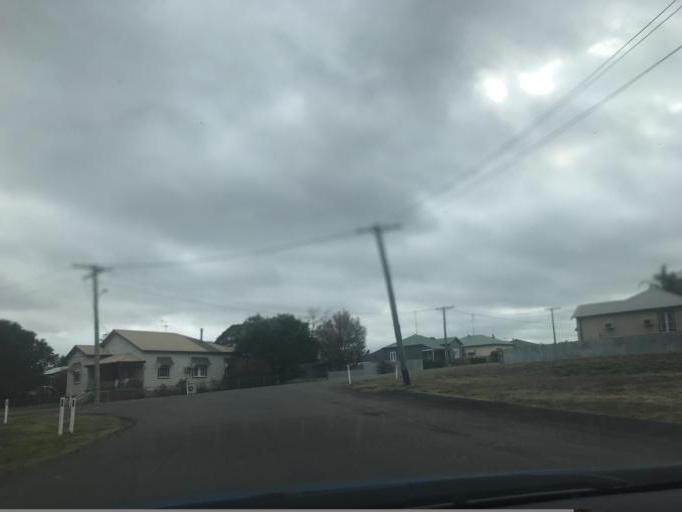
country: AU
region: New South Wales
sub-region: Cessnock
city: Cessnock
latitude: -32.9028
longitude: 151.2831
